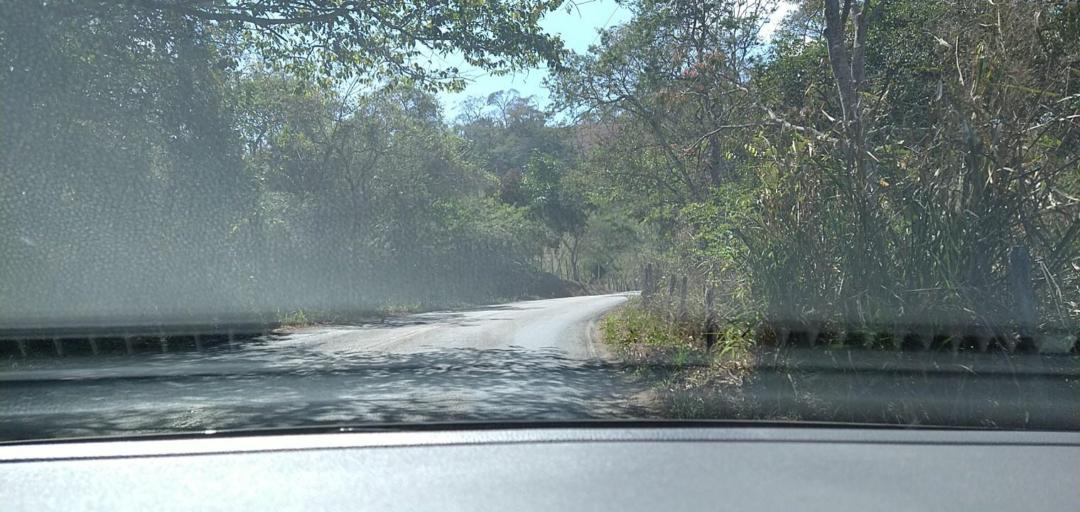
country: BR
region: Minas Gerais
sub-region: Ponte Nova
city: Ponte Nova
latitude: -20.2732
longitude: -42.9028
